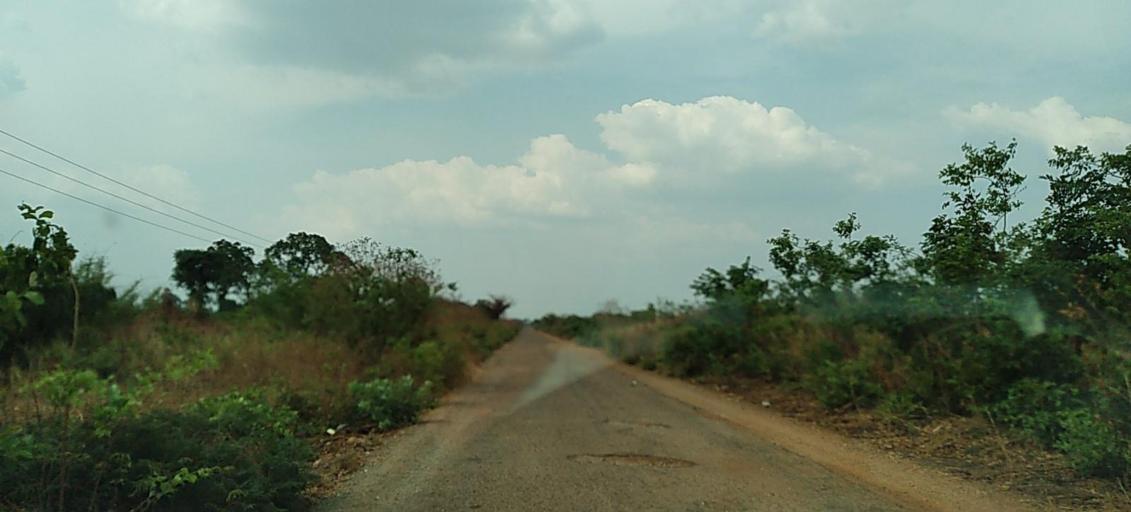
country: ZM
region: Copperbelt
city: Chililabombwe
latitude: -12.3881
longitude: 27.8083
